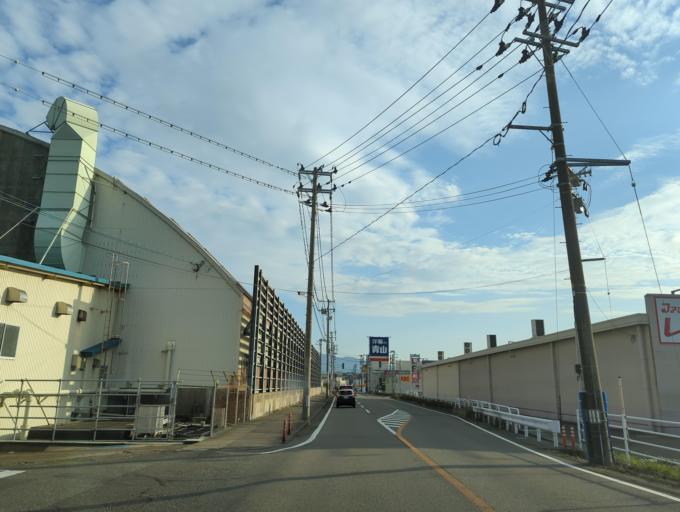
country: JP
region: Niigata
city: Kashiwazaki
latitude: 37.3633
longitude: 138.5635
